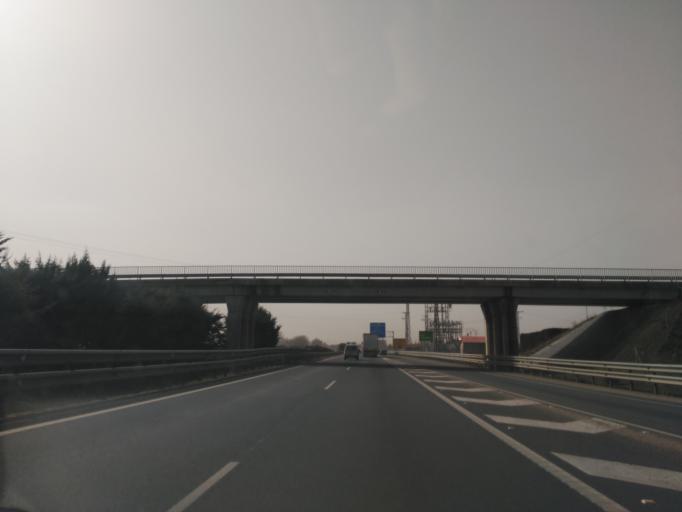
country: ES
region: Castille and Leon
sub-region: Provincia de Valladolid
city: Cabezon
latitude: 41.7428
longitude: -4.6613
